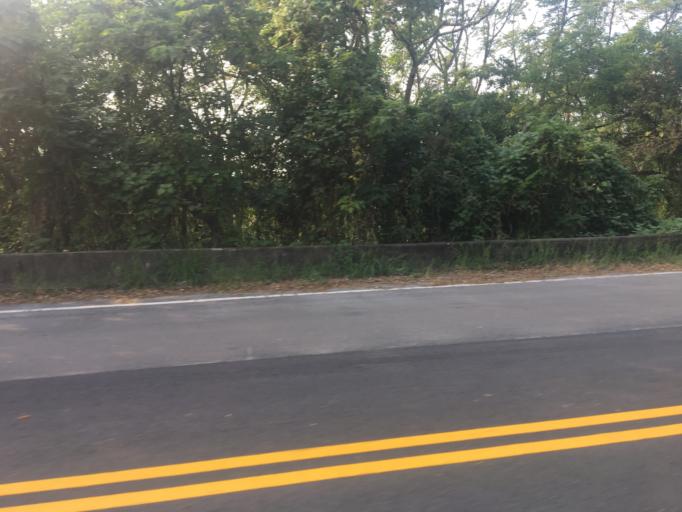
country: TW
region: Taiwan
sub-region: Hsinchu
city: Hsinchu
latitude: 24.7606
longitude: 120.9497
